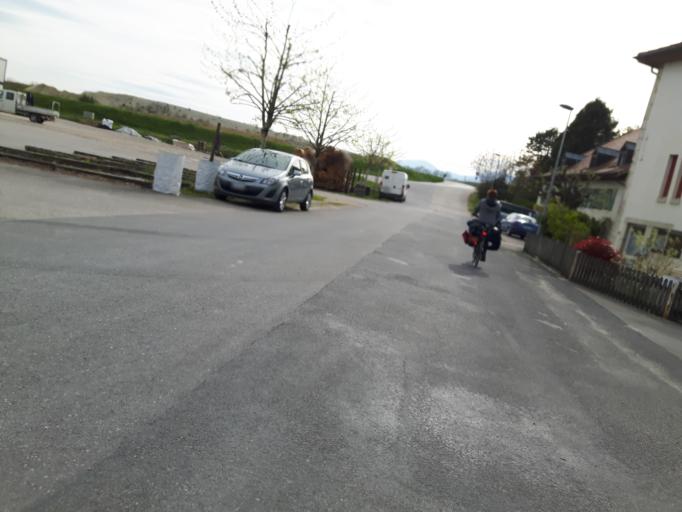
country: CH
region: Vaud
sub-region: Jura-Nord vaudois District
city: Grandson
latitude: 46.8282
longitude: 6.6766
